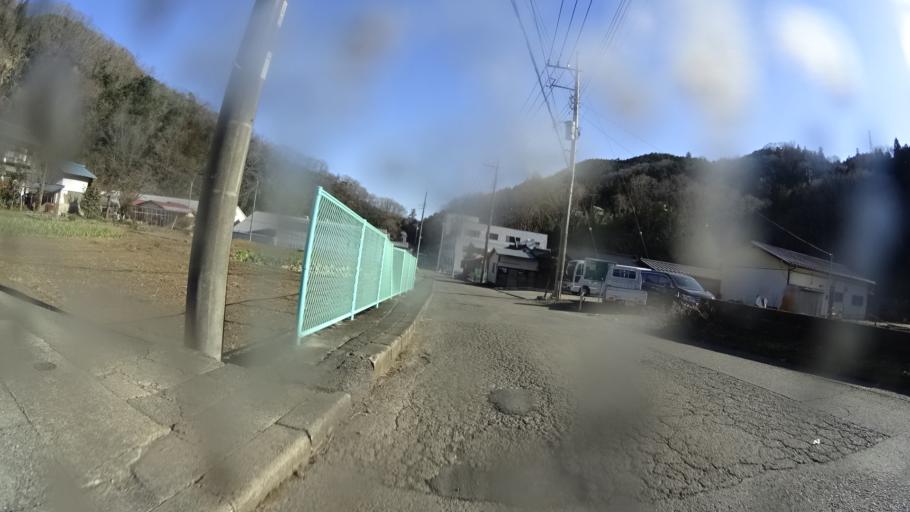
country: JP
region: Yamanashi
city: Uenohara
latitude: 35.6217
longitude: 139.1533
